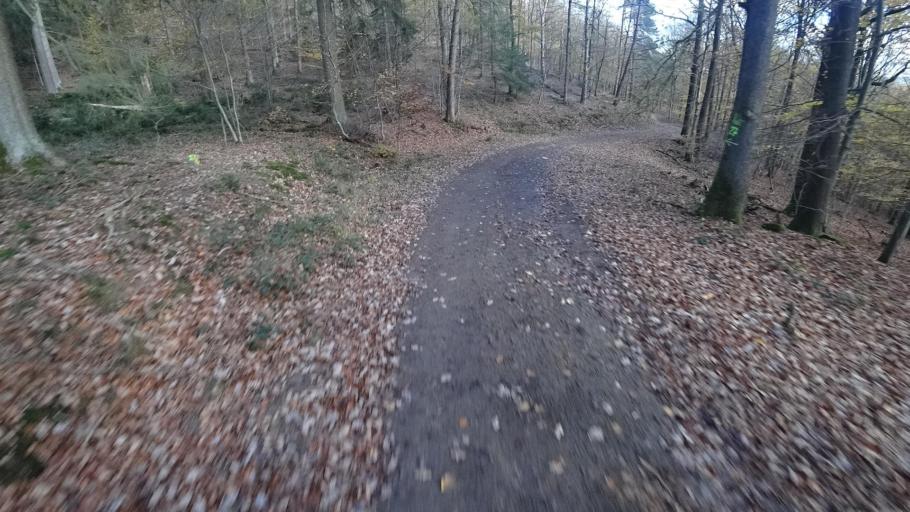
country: DE
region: Rheinland-Pfalz
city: Honningen
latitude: 50.4837
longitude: 6.9478
